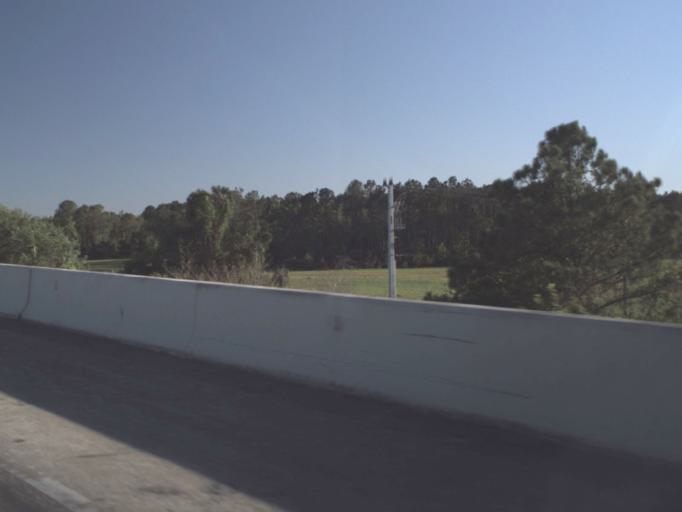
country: US
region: Florida
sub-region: Flagler County
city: Flagler Beach
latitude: 29.4975
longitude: -81.1922
